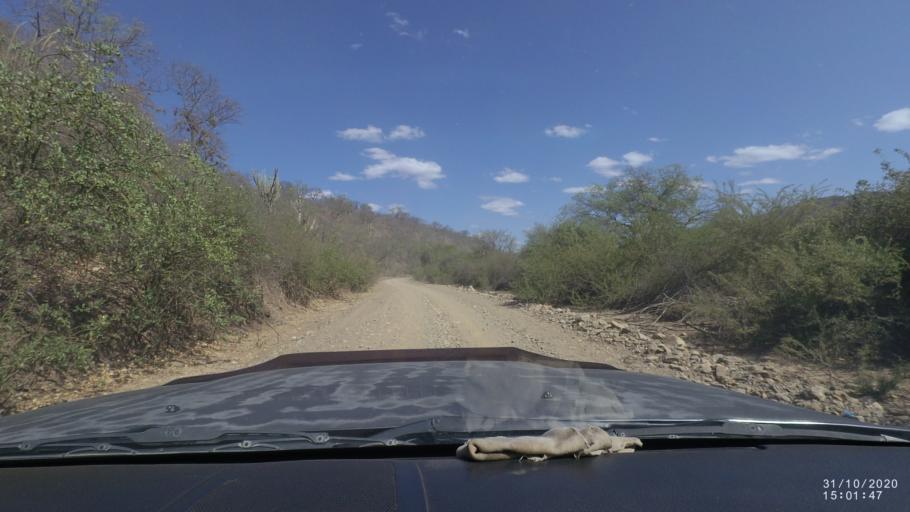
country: BO
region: Cochabamba
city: Aiquile
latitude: -18.2655
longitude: -64.8165
